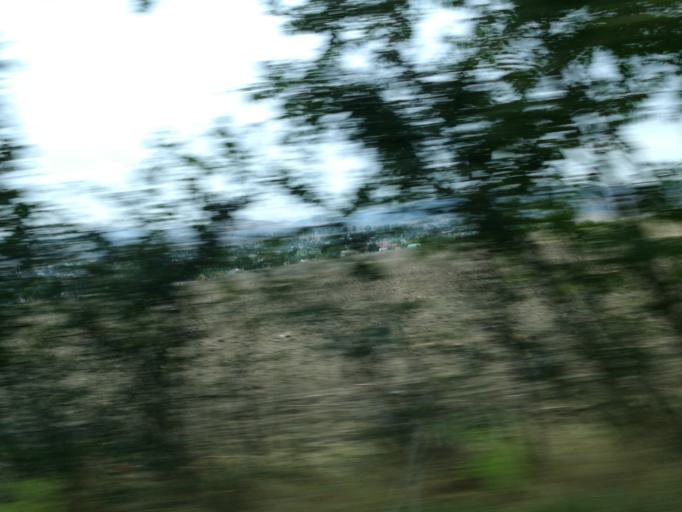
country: RO
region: Tulcea
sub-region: Comuna Horia
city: Horia
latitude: 45.0181
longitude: 28.4474
